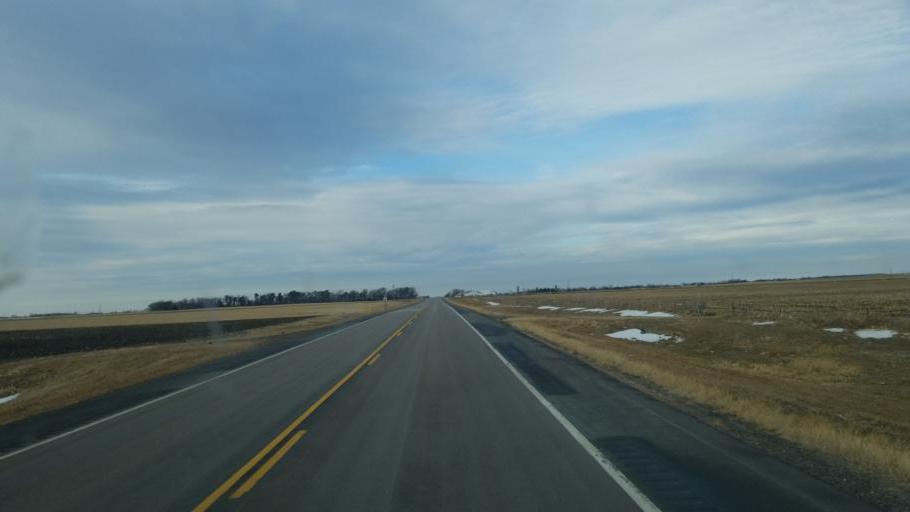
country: US
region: South Dakota
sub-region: Hutchinson County
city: Olivet
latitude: 43.0824
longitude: -97.6704
